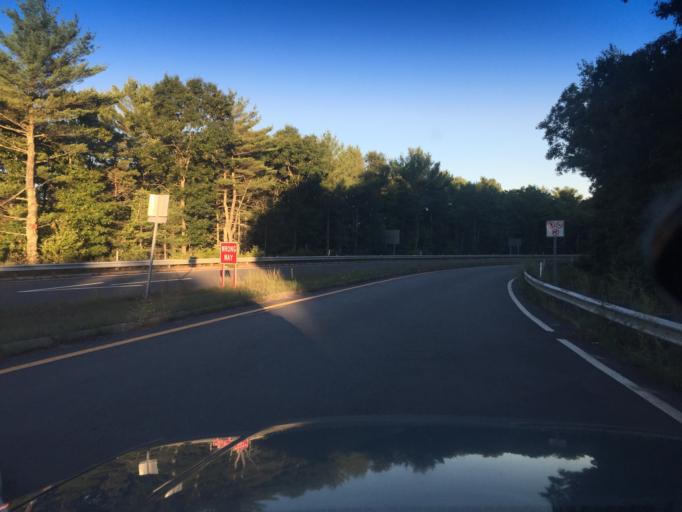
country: US
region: Massachusetts
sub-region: Plymouth County
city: West Wareham
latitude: 41.8074
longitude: -70.7681
